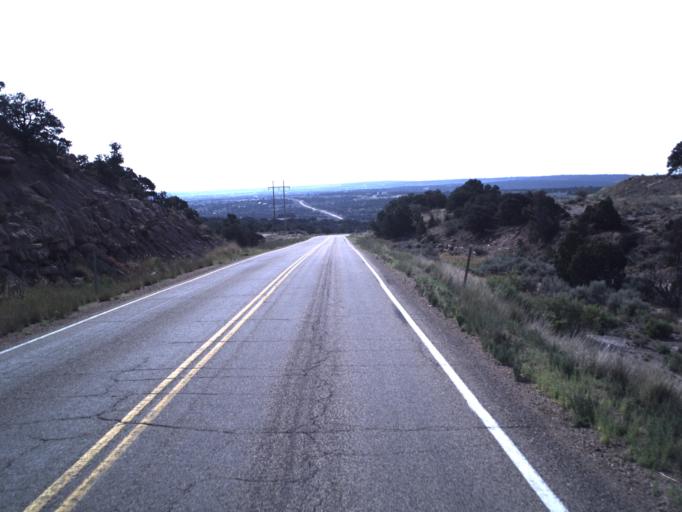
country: US
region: Utah
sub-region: Duchesne County
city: Duchesne
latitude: 40.3138
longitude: -110.3818
